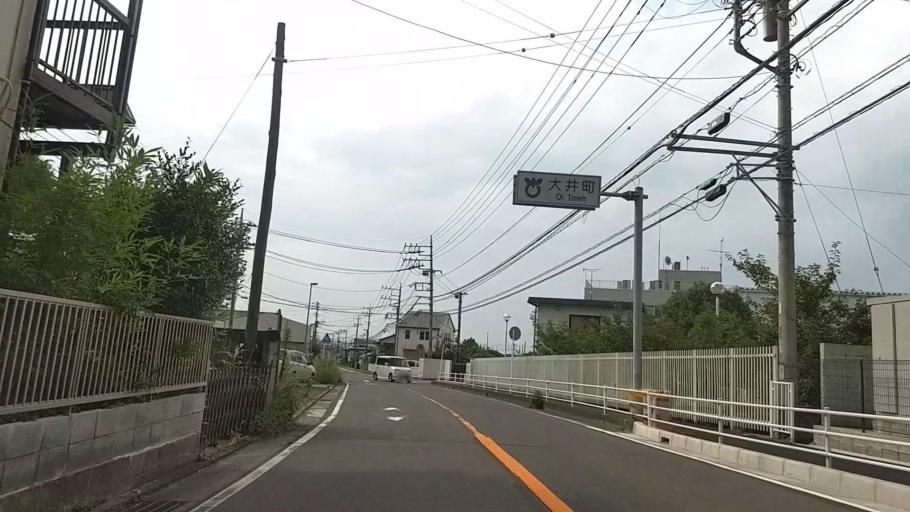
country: JP
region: Kanagawa
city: Hadano
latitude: 35.3442
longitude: 139.1507
